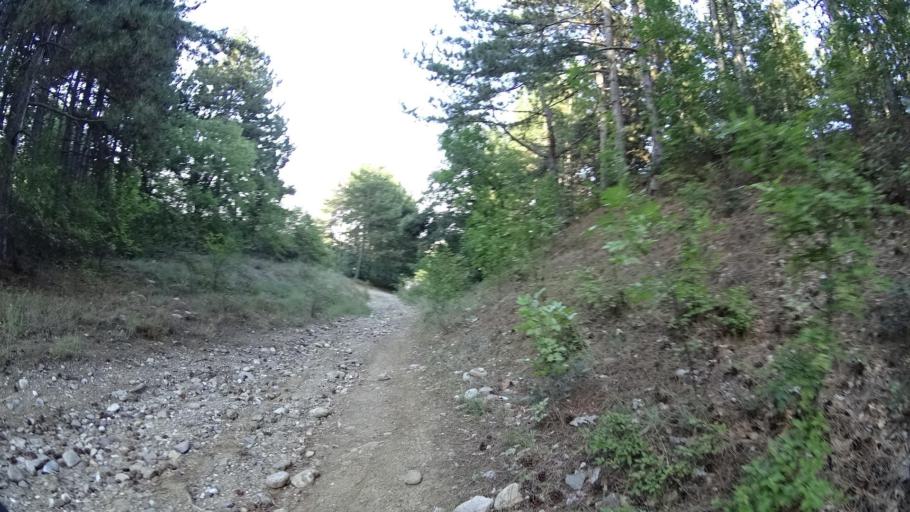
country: BG
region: Plovdiv
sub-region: Obshtina Plovdiv
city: Plovdiv
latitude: 42.0590
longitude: 24.6974
